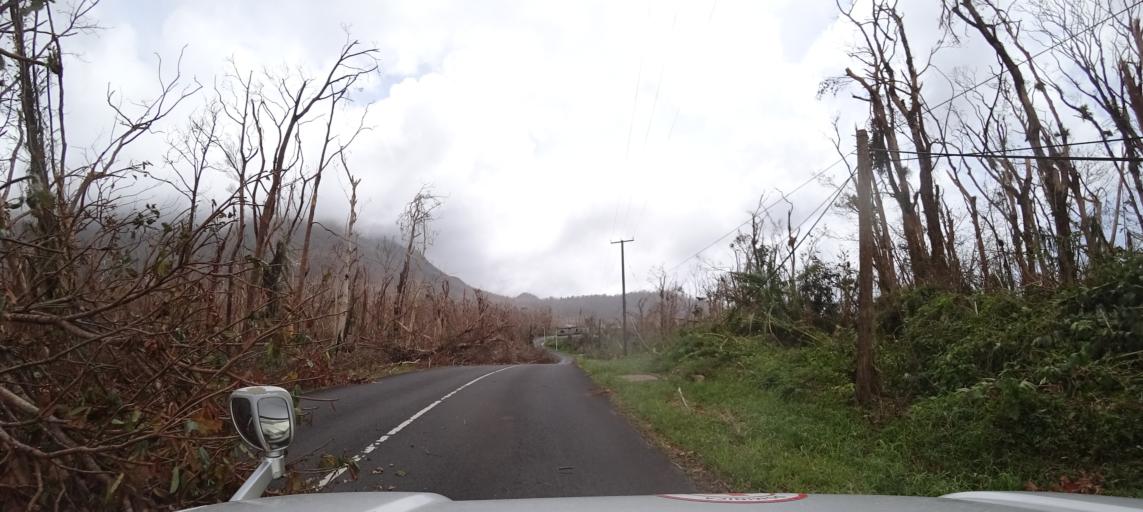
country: DM
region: Saint Paul
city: Pont Casse
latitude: 15.3858
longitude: -61.3447
